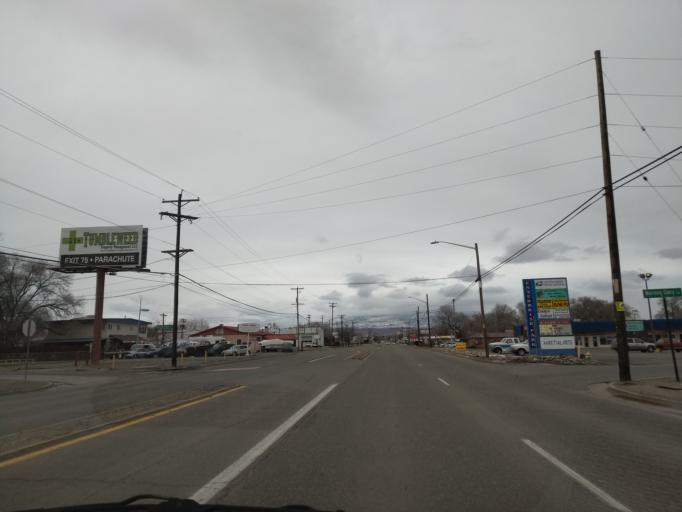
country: US
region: Colorado
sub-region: Mesa County
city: Fruitvale
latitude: 39.0773
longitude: -108.5121
